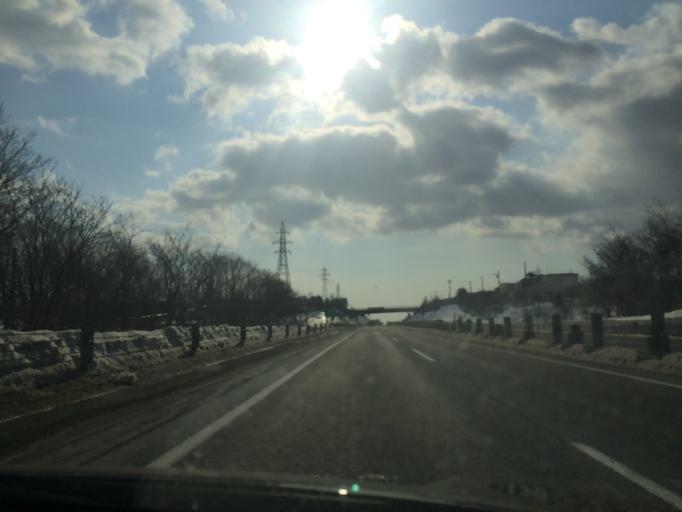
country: JP
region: Hokkaido
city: Kitahiroshima
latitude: 42.9683
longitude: 141.4904
